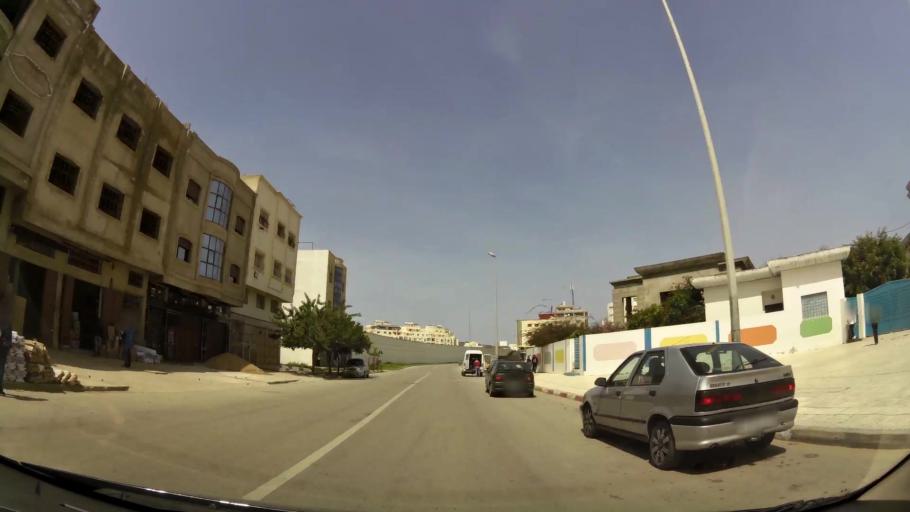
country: MA
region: Tanger-Tetouan
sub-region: Tanger-Assilah
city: Tangier
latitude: 35.7579
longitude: -5.8408
